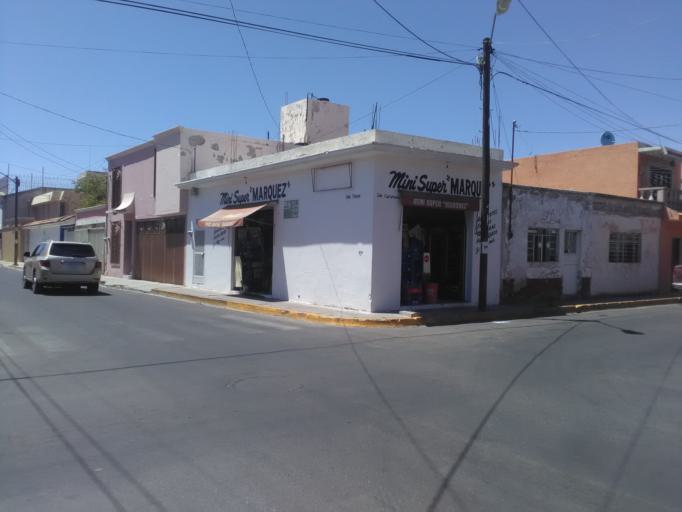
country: MX
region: Durango
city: Victoria de Durango
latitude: 24.0307
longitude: -104.6628
